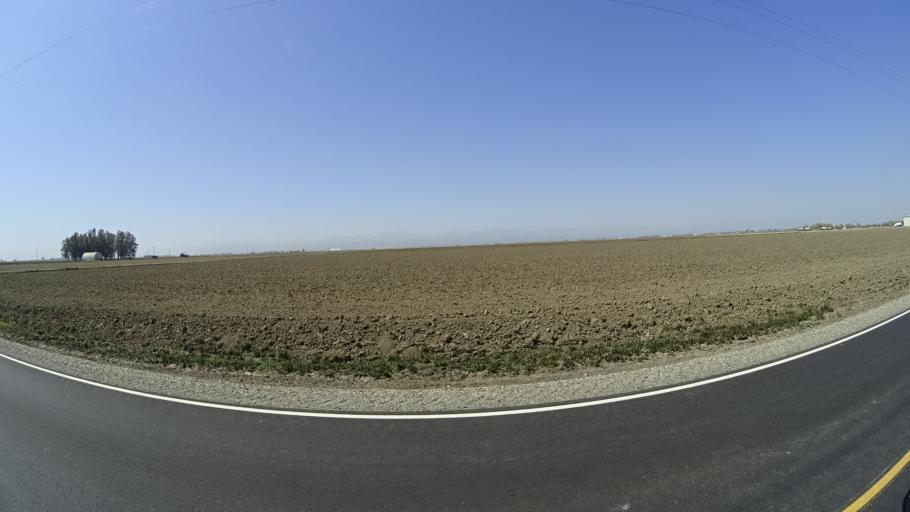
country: US
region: California
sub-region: Glenn County
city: Willows
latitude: 39.4775
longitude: -122.1364
